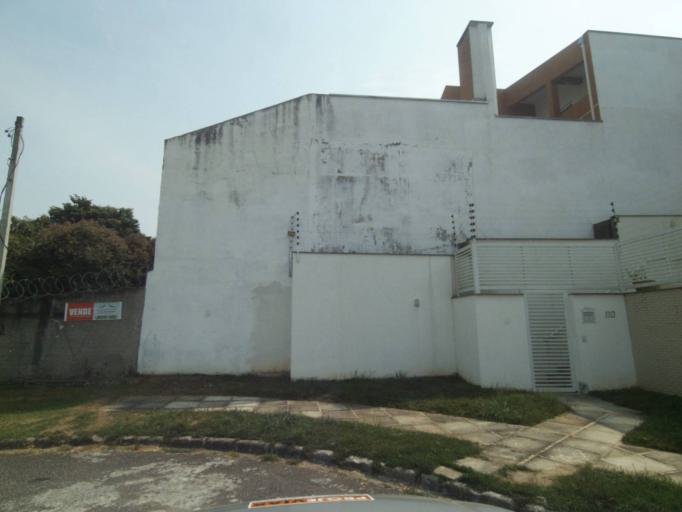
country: BR
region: Parana
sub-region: Pinhais
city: Pinhais
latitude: -25.4776
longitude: -49.2231
